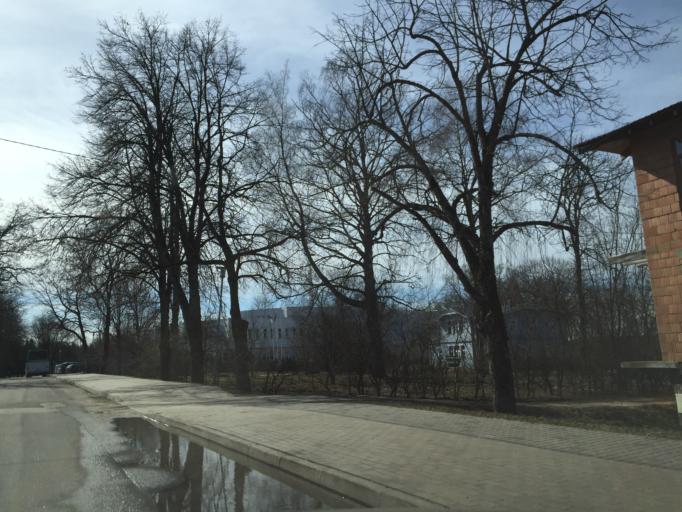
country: LV
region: Sigulda
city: Sigulda
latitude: 57.1536
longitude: 24.8469
